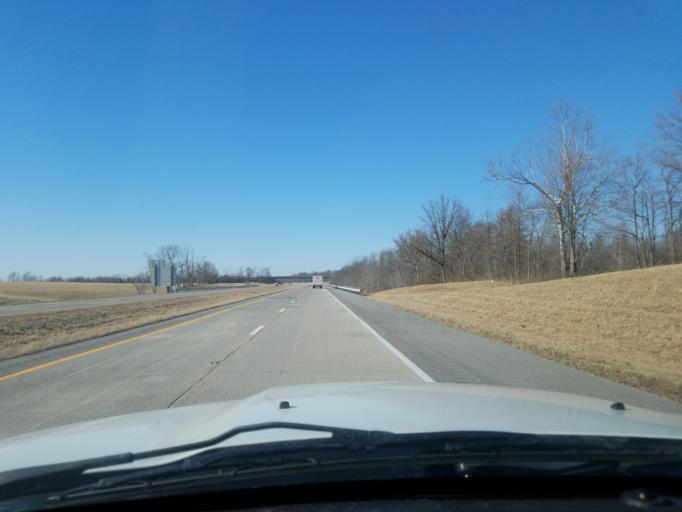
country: US
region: Indiana
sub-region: Warrick County
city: Newburgh
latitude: 37.7672
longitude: -87.4248
